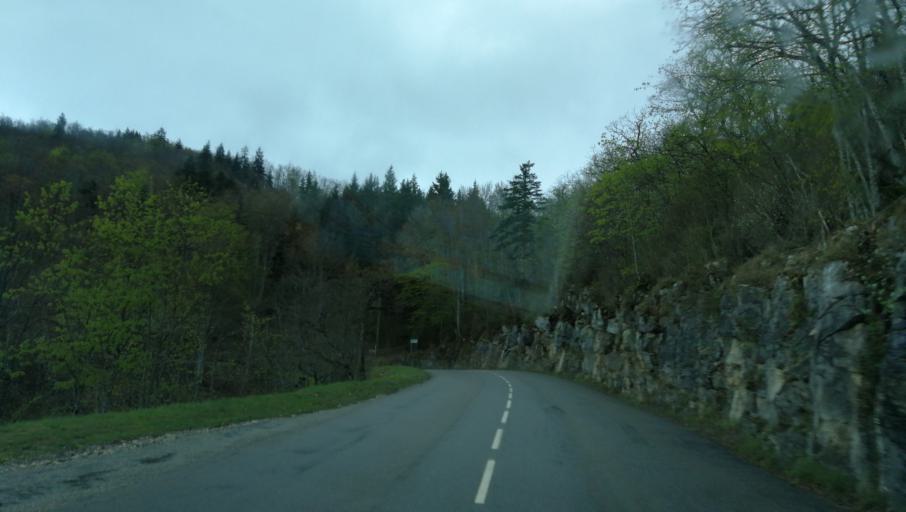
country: FR
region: Rhone-Alpes
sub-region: Departement de la Drome
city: Saint-Laurent-en-Royans
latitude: 45.0028
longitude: 5.3300
